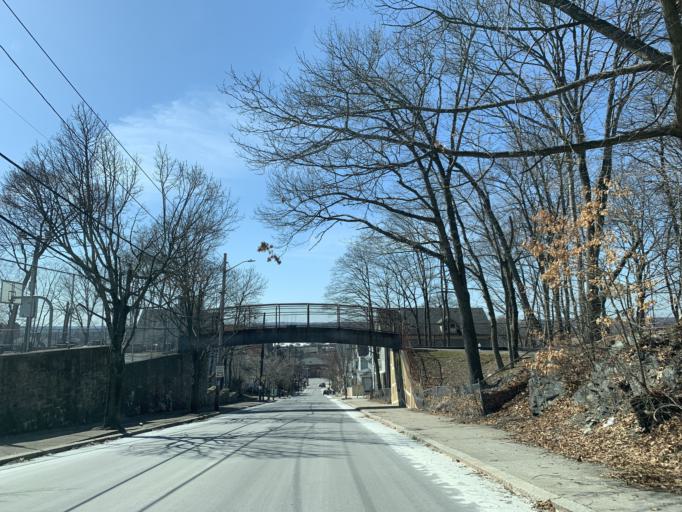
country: US
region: Rhode Island
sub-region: Providence County
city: Providence
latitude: 41.8423
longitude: -71.4037
